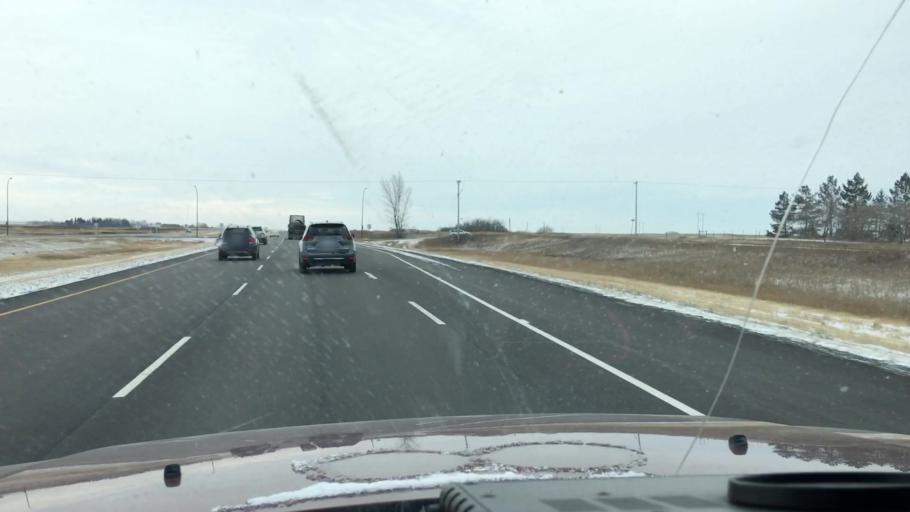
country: CA
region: Saskatchewan
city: Saskatoon
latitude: 51.8544
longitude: -106.5084
